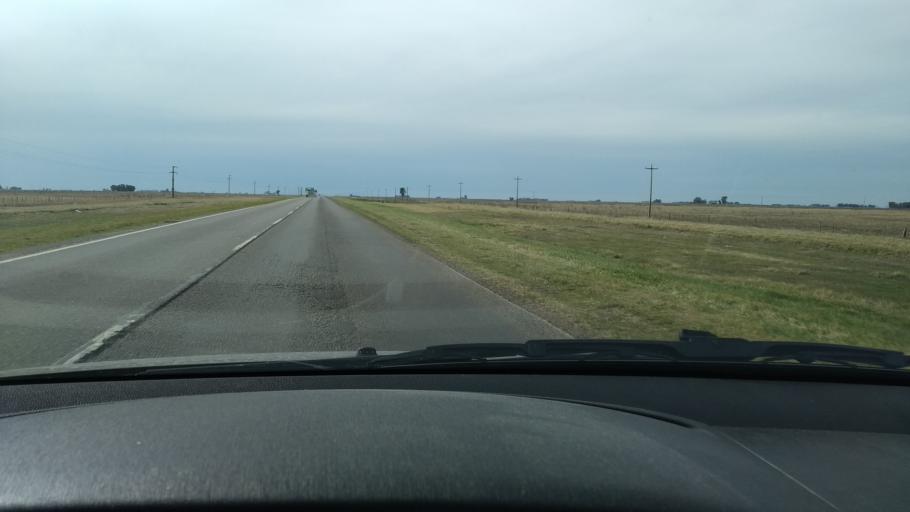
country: AR
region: Buenos Aires
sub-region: Partido de Azul
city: Azul
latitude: -36.6954
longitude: -59.7441
